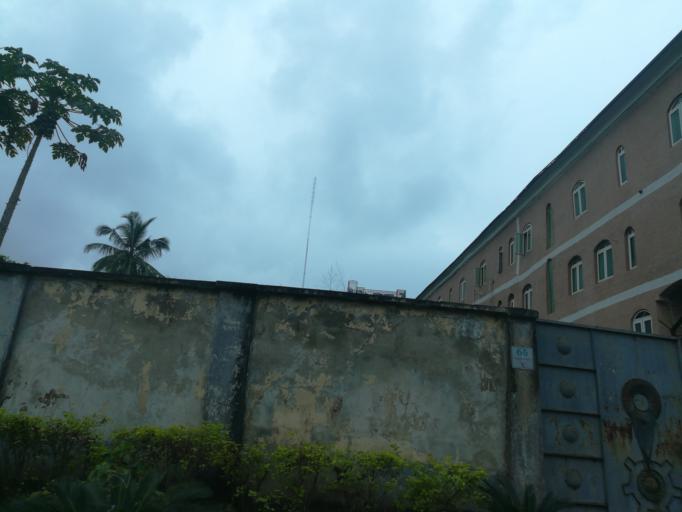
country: NG
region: Lagos
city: Oshodi
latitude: 6.5721
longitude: 3.3488
